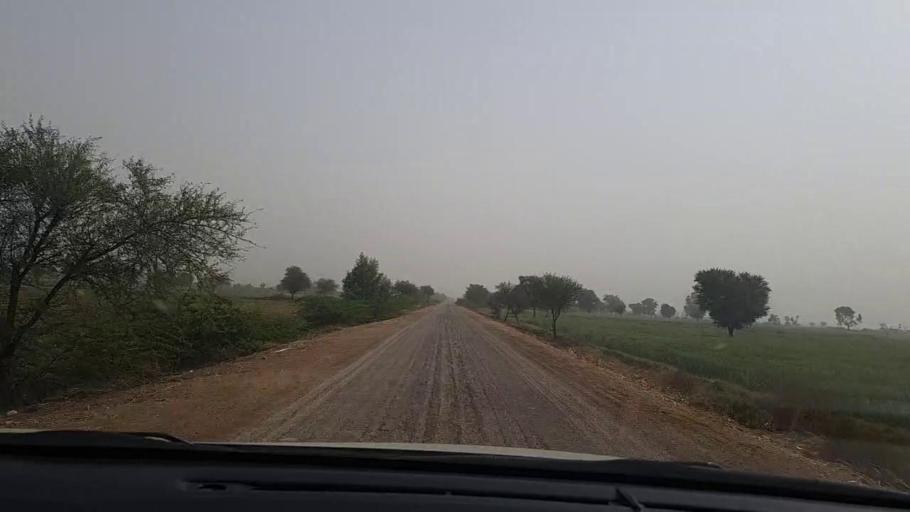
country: PK
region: Sindh
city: Pithoro
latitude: 25.4004
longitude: 69.3210
